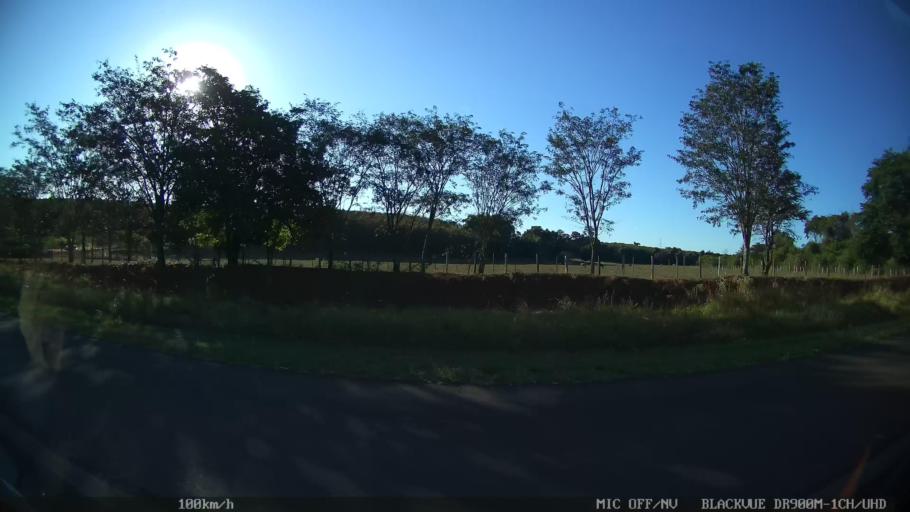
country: BR
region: Sao Paulo
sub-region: Guapiacu
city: Guapiacu
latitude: -20.7686
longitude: -49.2078
